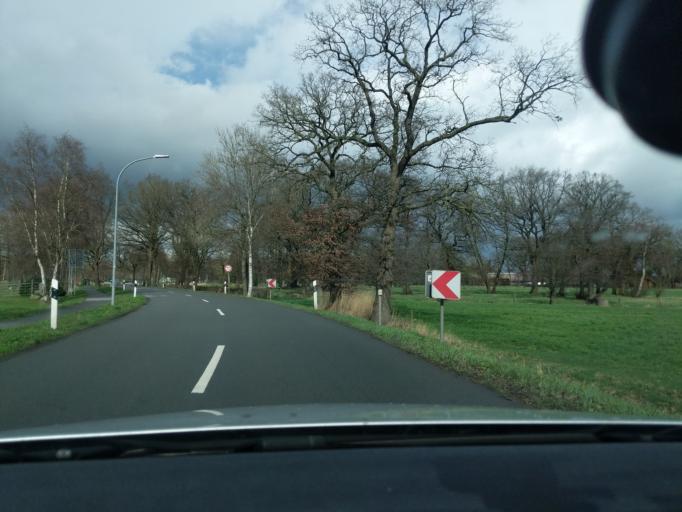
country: DE
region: Lower Saxony
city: Stade
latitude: 53.6280
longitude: 9.4320
